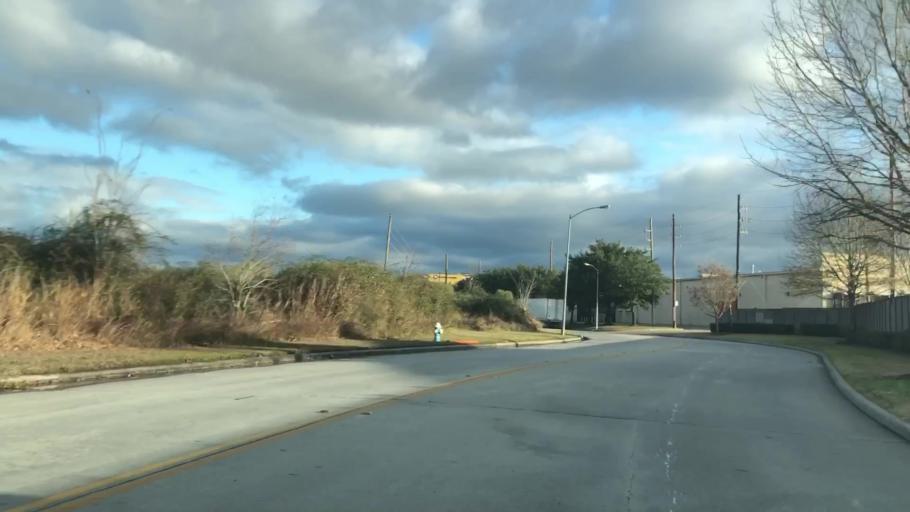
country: US
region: Texas
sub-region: Harris County
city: Aldine
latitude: 29.9188
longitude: -95.4165
